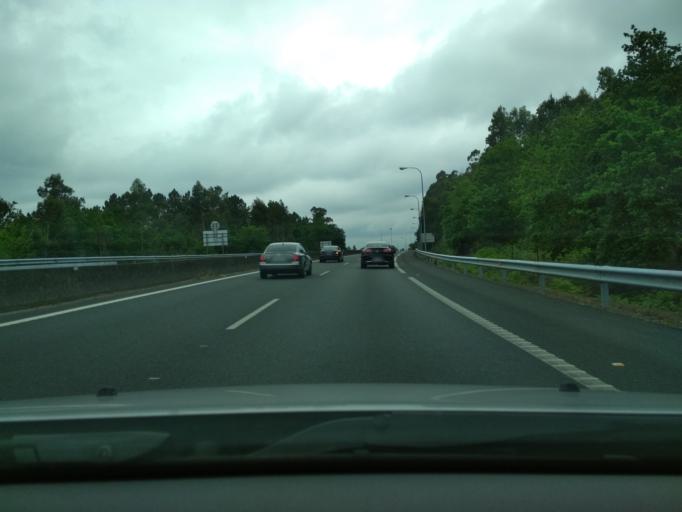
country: ES
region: Galicia
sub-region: Provincia da Coruna
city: Santiago de Compostela
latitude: 42.8122
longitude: -8.5796
